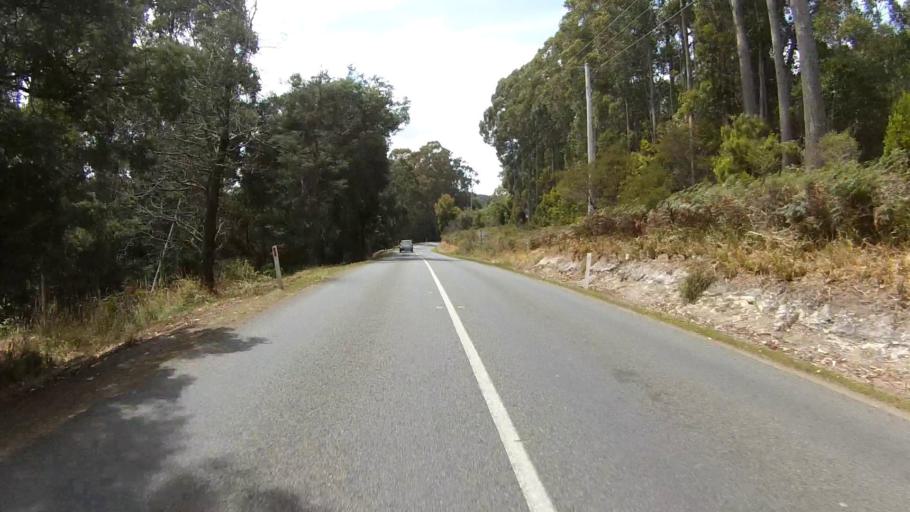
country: AU
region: Tasmania
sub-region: Kingborough
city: Kettering
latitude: -43.1063
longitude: 147.2355
